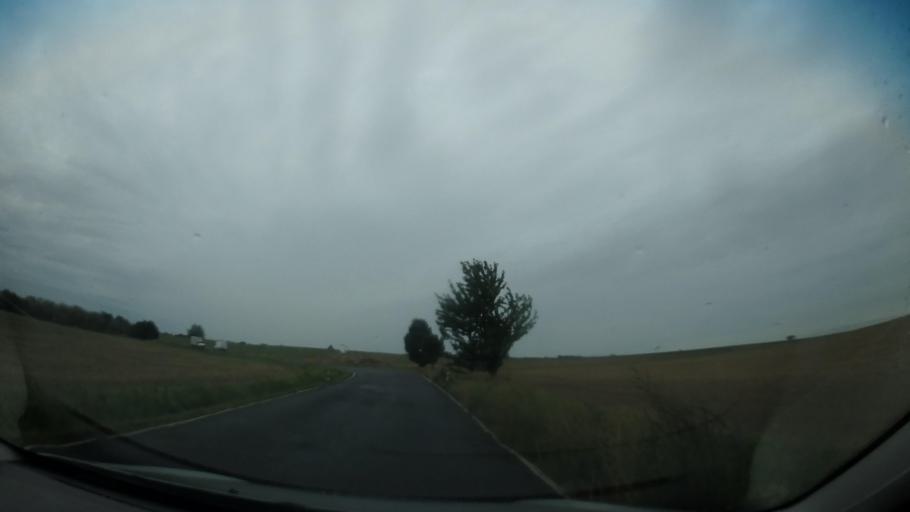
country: CZ
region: Central Bohemia
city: Loucen
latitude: 50.2517
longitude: 15.0226
